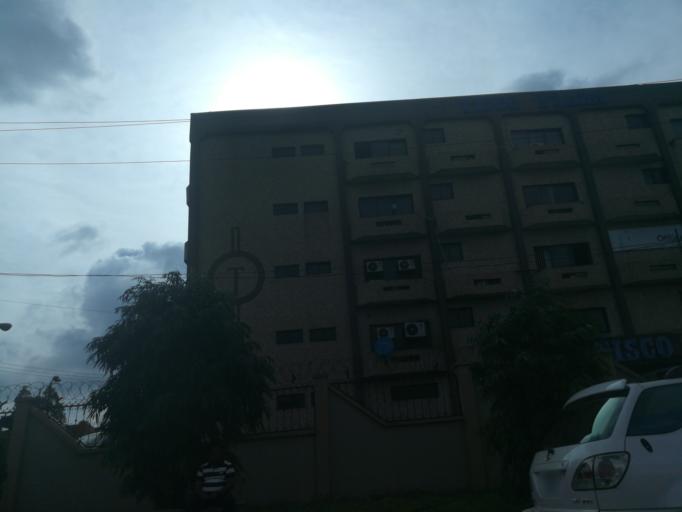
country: NG
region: Lagos
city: Ikeja
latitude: 6.6206
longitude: 3.3564
